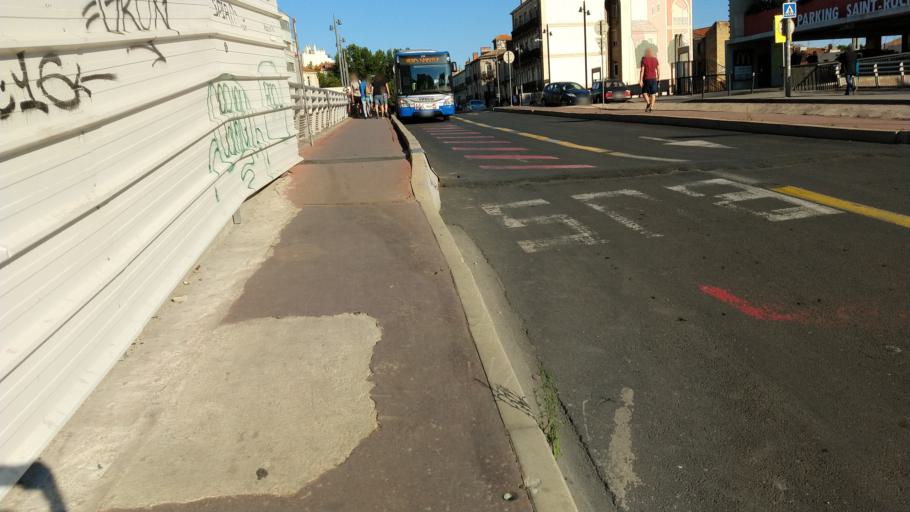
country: FR
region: Languedoc-Roussillon
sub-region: Departement de l'Herault
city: Montpellier
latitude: 43.6041
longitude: 3.8788
